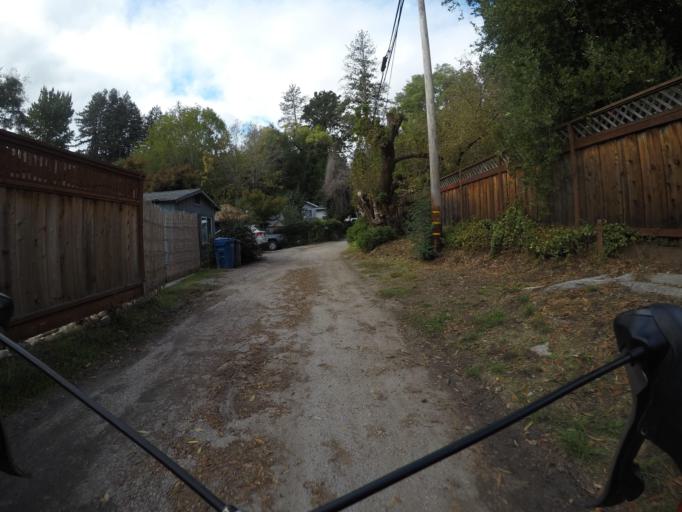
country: US
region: California
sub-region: Santa Cruz County
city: Ben Lomond
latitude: 37.0827
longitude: -122.0819
